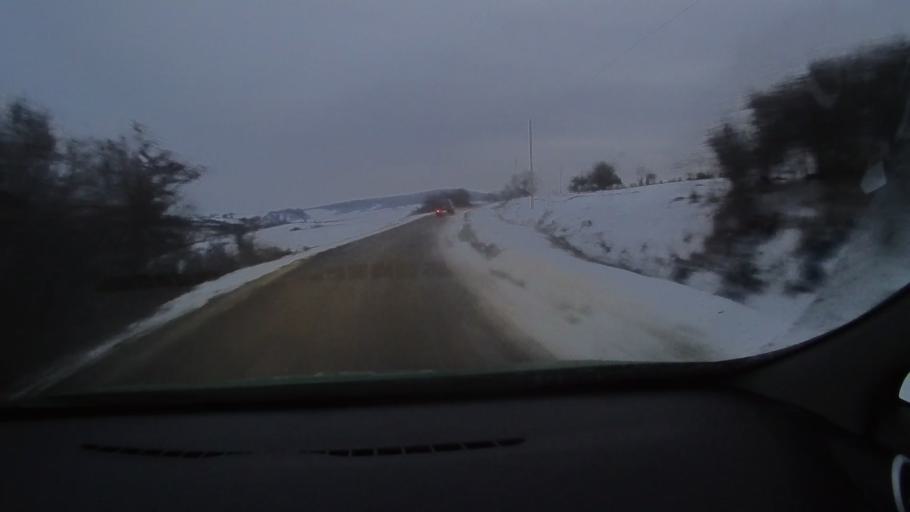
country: RO
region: Harghita
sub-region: Comuna Darjiu
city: Darjiu
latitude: 46.1924
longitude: 25.2450
